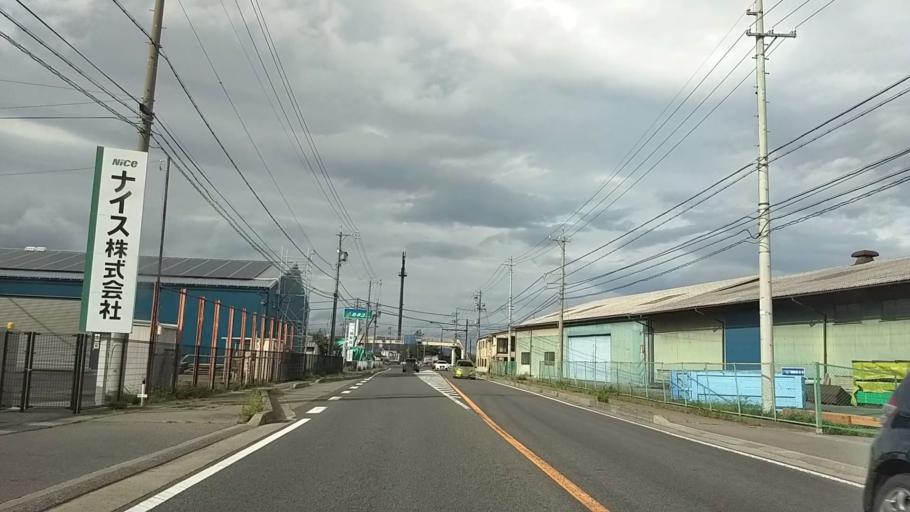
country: JP
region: Nagano
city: Suzaka
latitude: 36.6741
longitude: 138.2667
